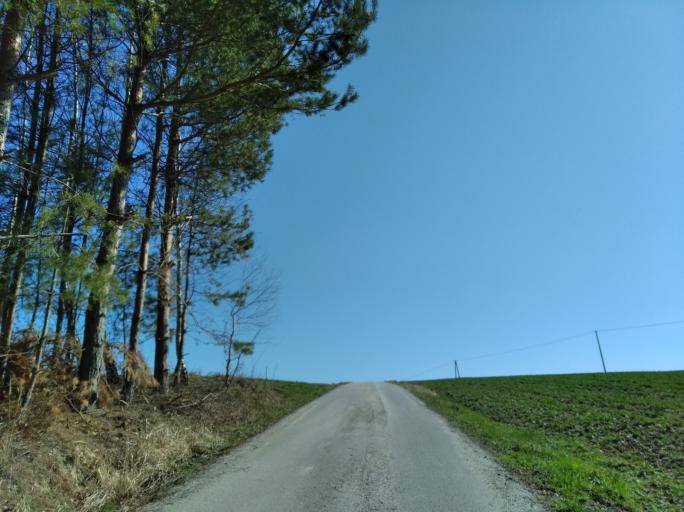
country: PL
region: Subcarpathian Voivodeship
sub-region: Powiat strzyzowski
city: Strzyzow
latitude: 49.8568
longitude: 21.8133
